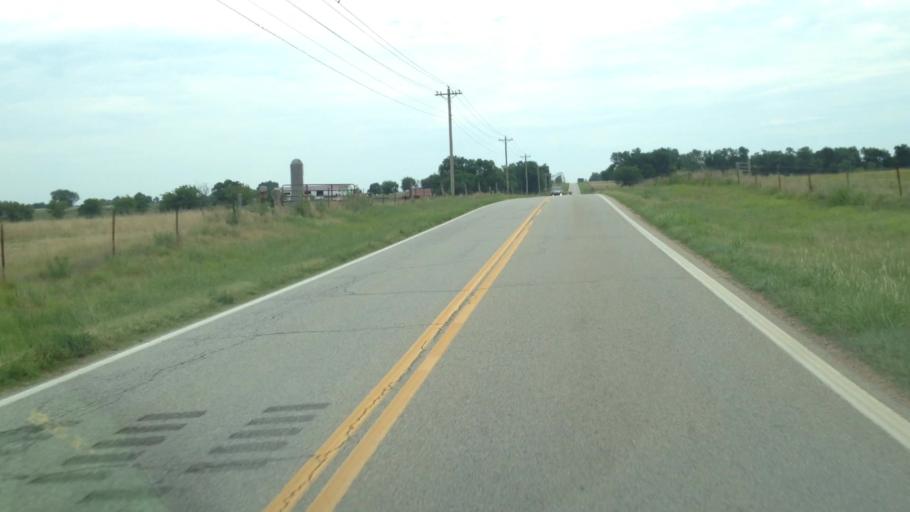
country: US
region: Oklahoma
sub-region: Delaware County
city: Cleora
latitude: 36.6003
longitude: -94.9634
